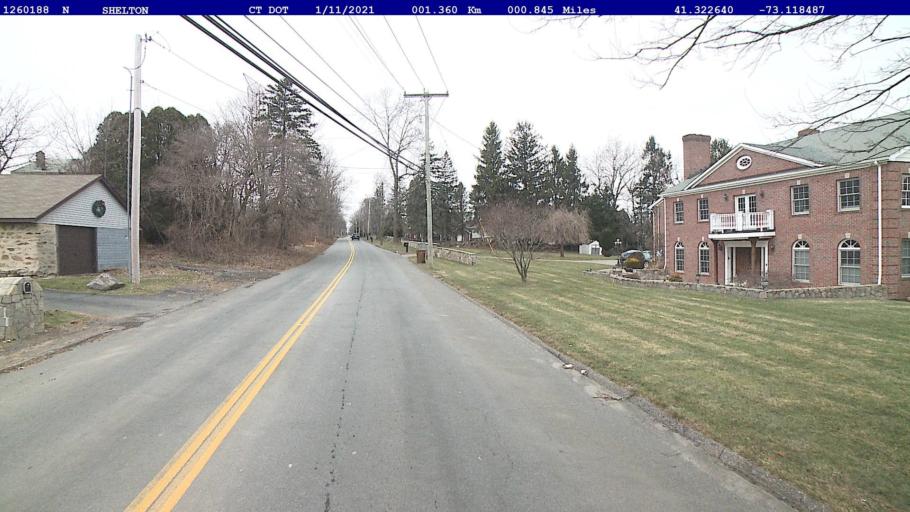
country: US
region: Connecticut
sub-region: Fairfield County
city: Shelton
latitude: 41.3226
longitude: -73.1185
